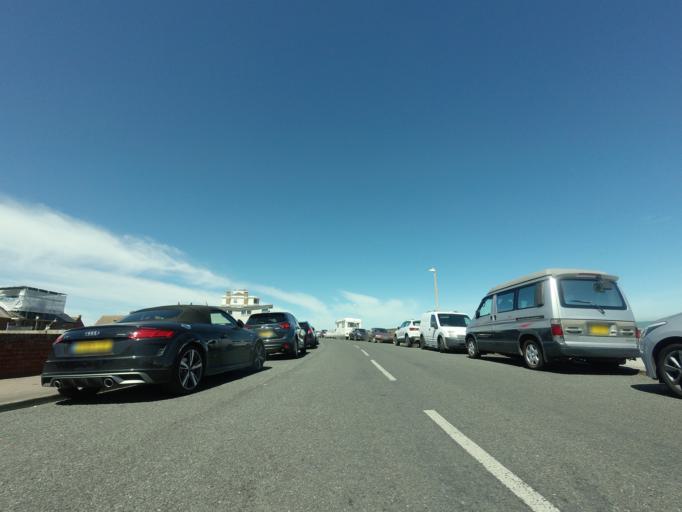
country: GB
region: England
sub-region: Kent
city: Deal
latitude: 51.2315
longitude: 1.4042
